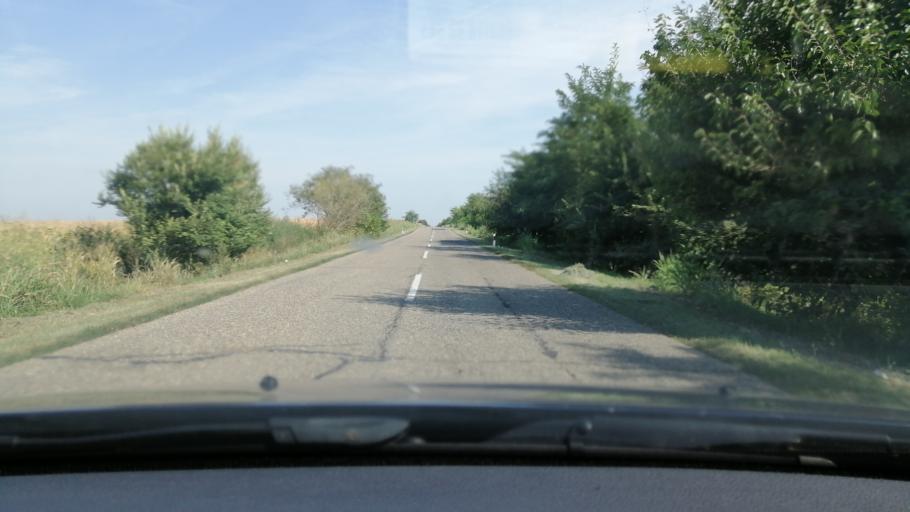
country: RS
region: Autonomna Pokrajina Vojvodina
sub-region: Juznobanatski Okrug
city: Kovacica
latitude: 45.1342
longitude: 20.6162
